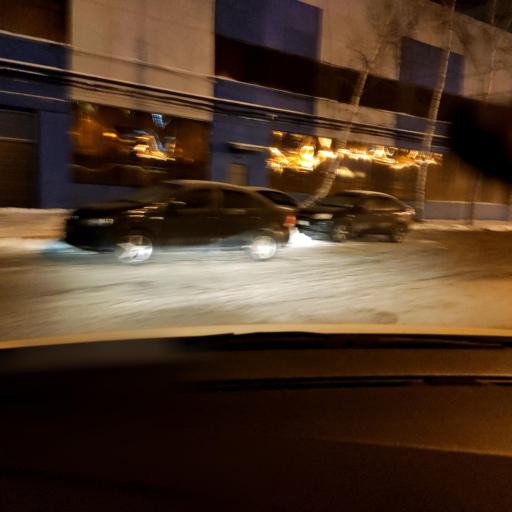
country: RU
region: Tatarstan
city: Staroye Arakchino
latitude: 55.8313
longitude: 49.0452
